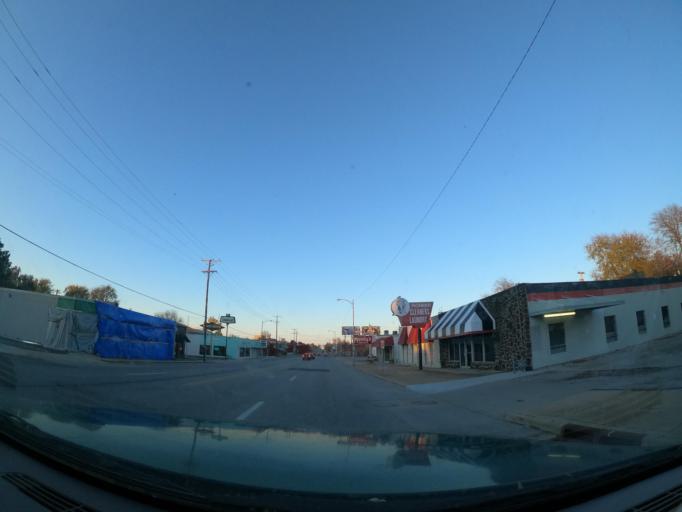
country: US
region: Oklahoma
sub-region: Tulsa County
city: Tulsa
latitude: 36.1460
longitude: -95.9403
